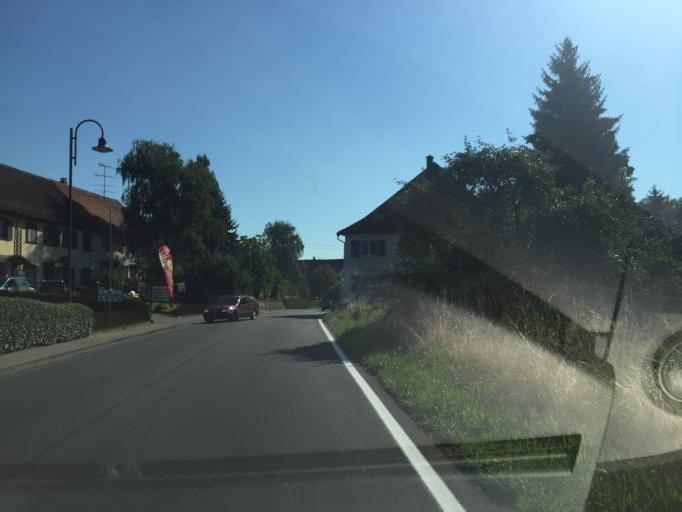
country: DE
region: Baden-Wuerttemberg
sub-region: Freiburg Region
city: Ohningen
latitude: 47.6602
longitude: 8.8823
